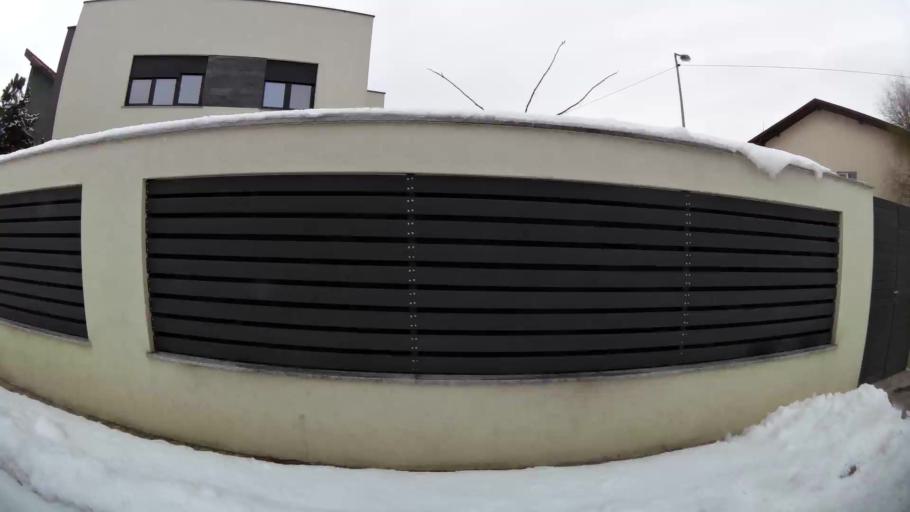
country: RO
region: Ilfov
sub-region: Comuna Tunari
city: Tunari
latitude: 44.5080
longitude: 26.1154
